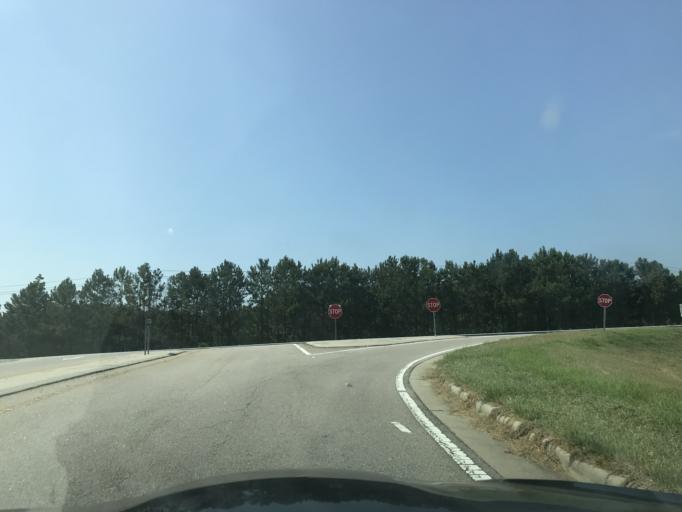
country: US
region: North Carolina
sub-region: Wilson County
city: Lucama
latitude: 35.6958
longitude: -77.9763
